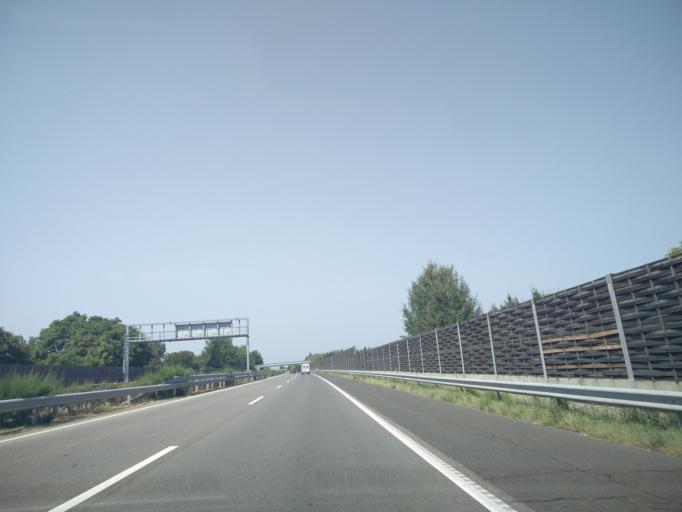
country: HU
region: Csongrad
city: Szatymaz
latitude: 46.3285
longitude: 20.0294
